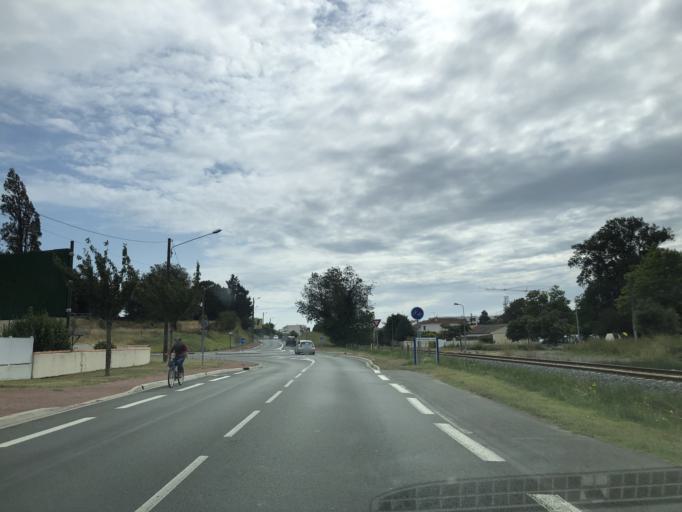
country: FR
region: Poitou-Charentes
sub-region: Departement de la Charente-Maritime
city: Royan
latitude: 45.6291
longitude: -1.0098
